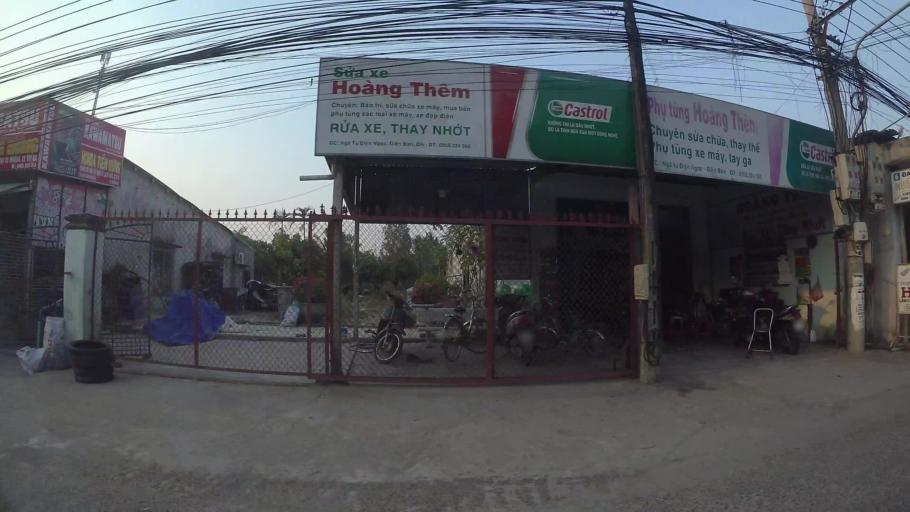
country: VN
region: Da Nang
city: Ngu Hanh Son
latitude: 15.9560
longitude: 108.2533
